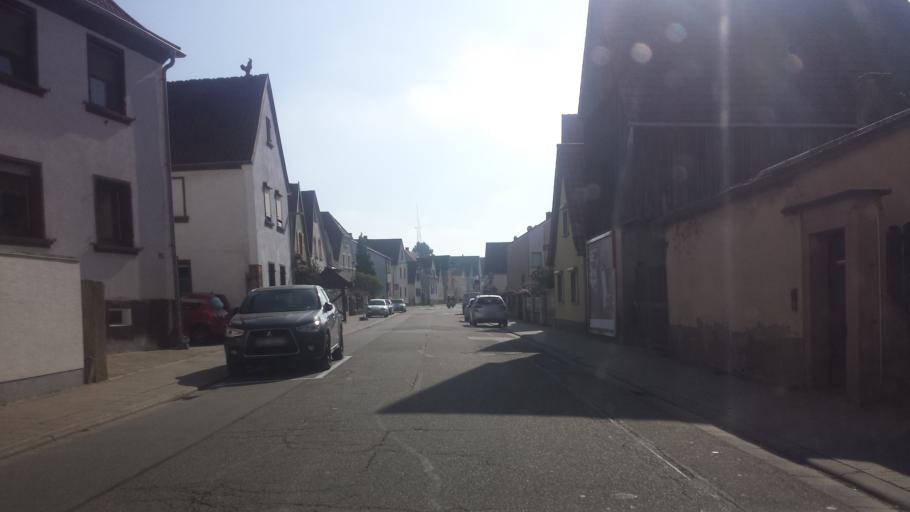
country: DE
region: Rheinland-Pfalz
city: Offenbach an der Queich
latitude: 49.1904
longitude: 8.1906
